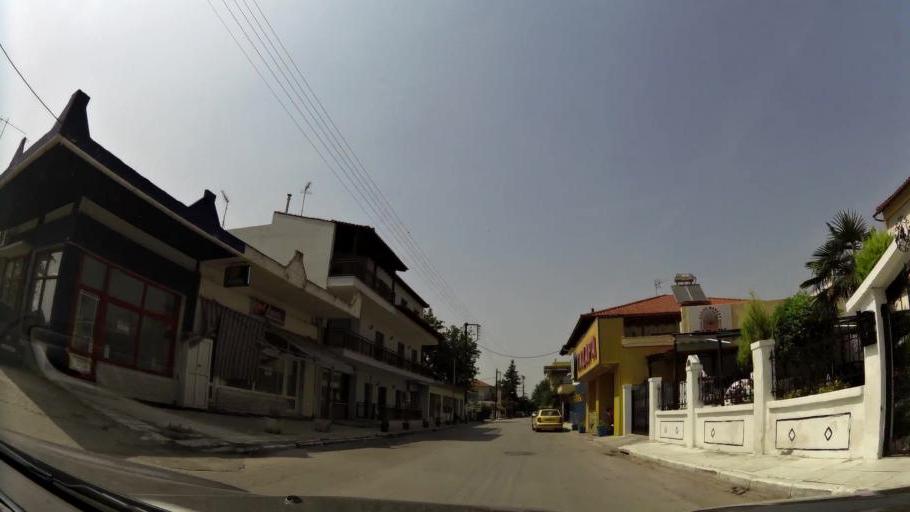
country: GR
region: Central Macedonia
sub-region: Nomos Thessalonikis
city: Nea Magnisia
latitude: 40.6878
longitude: 22.8421
